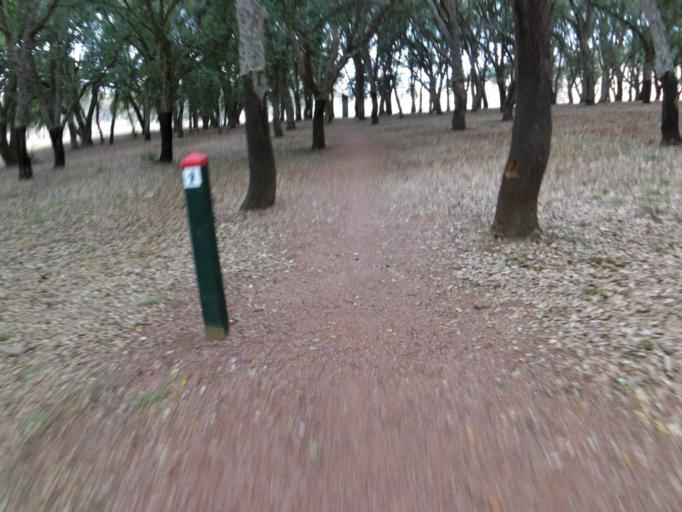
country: AU
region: Australian Capital Territory
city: Macquarie
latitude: -35.2831
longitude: 149.0811
